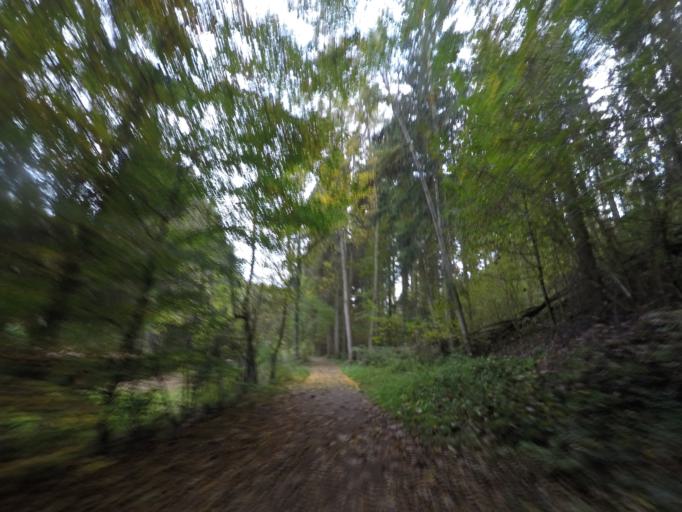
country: LU
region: Luxembourg
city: Itzig
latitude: 49.5971
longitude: 6.1599
